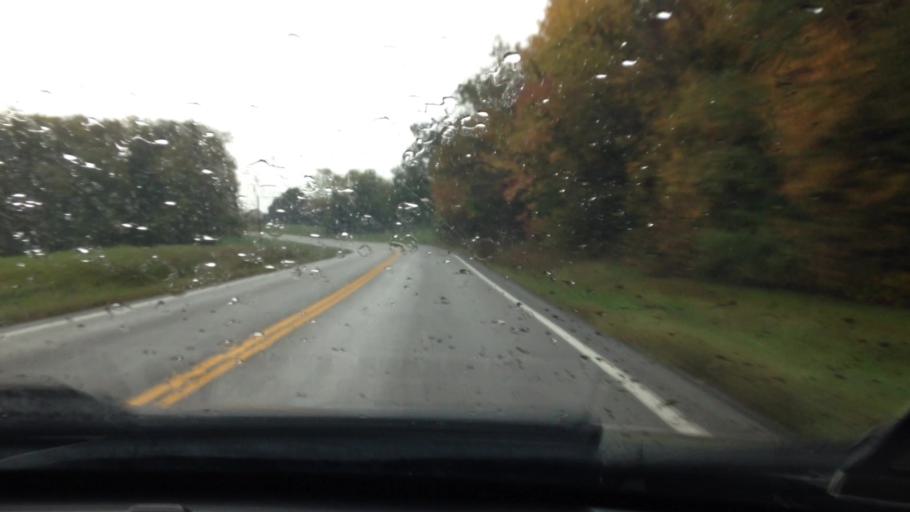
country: US
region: Missouri
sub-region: Platte County
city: Platte City
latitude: 39.3833
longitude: -94.8197
